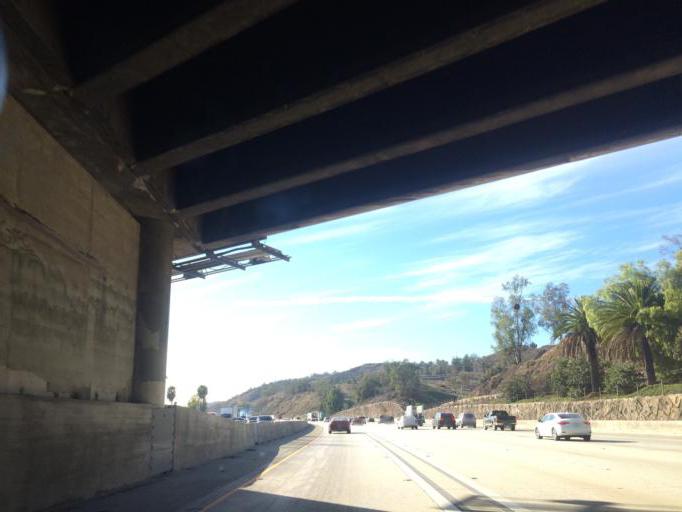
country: US
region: California
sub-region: Los Angeles County
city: La Verne
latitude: 34.0729
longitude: -117.7874
